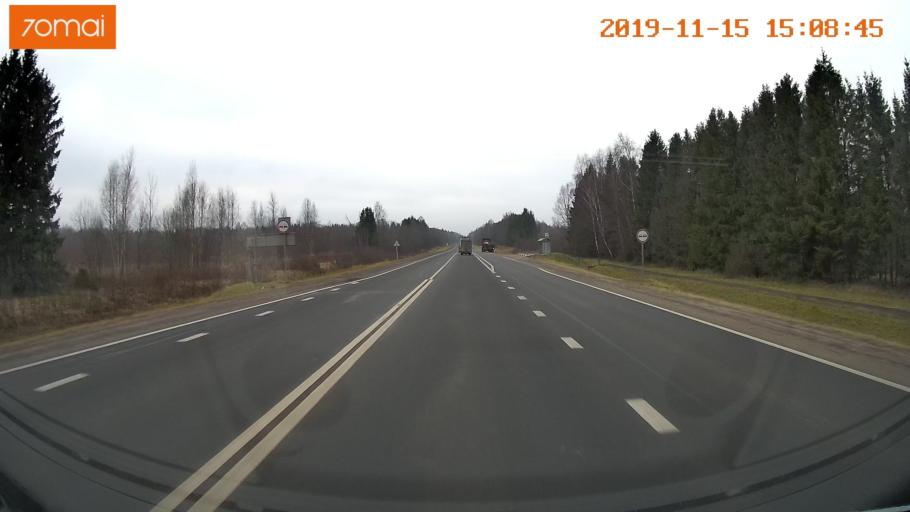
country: RU
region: Jaroslavl
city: Prechistoye
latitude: 58.3665
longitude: 40.2727
